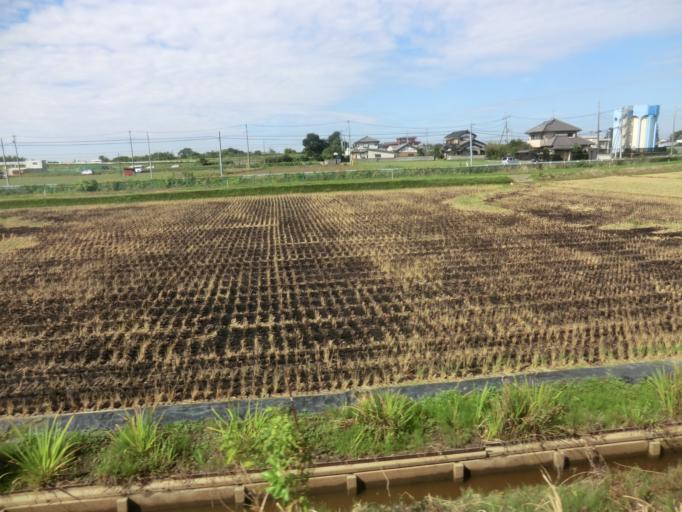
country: JP
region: Ibaraki
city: Ishige
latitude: 36.0787
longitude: 139.9813
